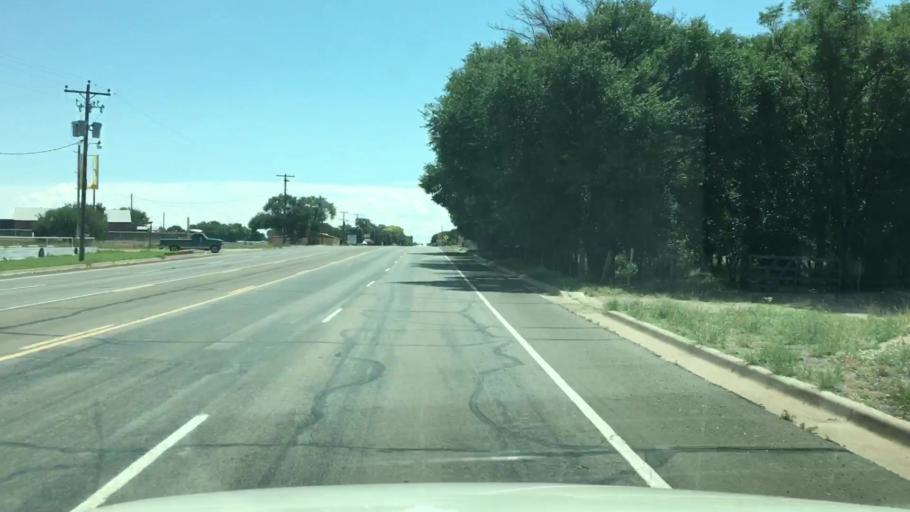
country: US
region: New Mexico
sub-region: De Baca County
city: Fort Sumner
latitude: 34.4679
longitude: -104.2338
